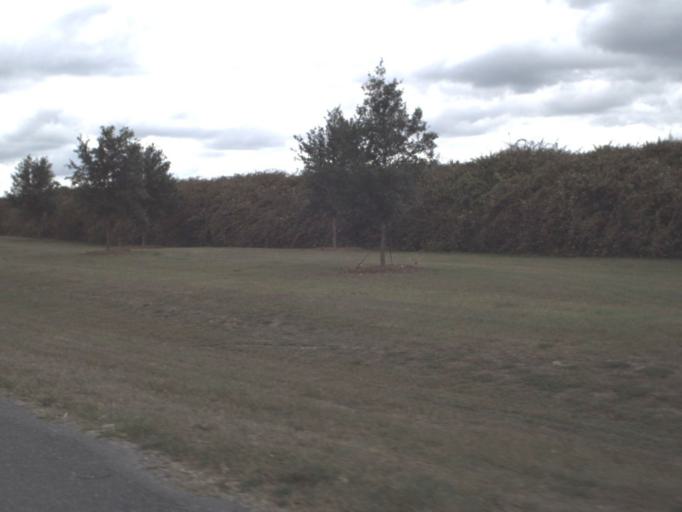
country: US
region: Florida
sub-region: Marion County
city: Ocala
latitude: 29.2595
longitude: -82.1378
